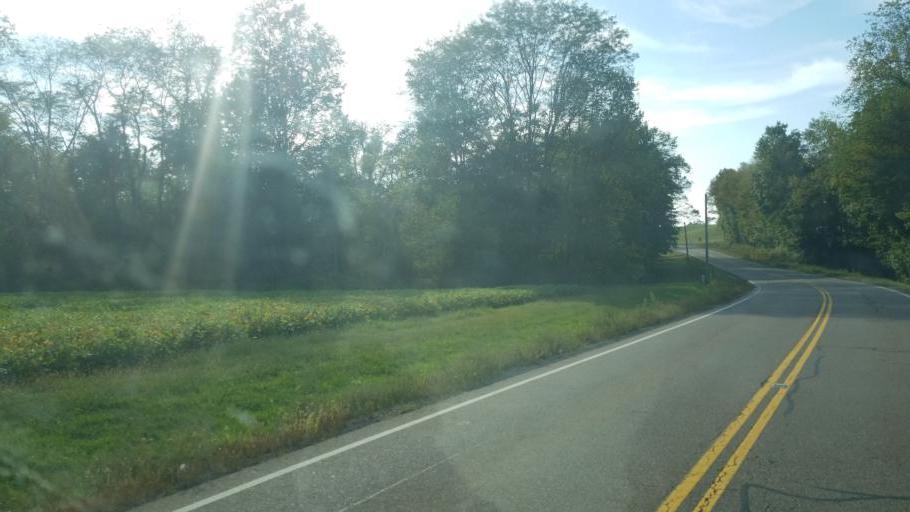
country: US
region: Ohio
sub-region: Knox County
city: Oak Hill
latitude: 40.4028
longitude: -82.2867
